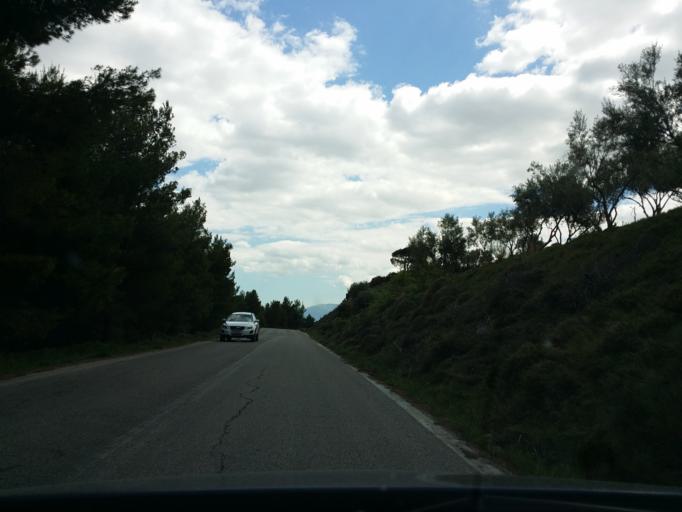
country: GR
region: Attica
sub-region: Nomarchia Dytikis Attikis
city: Fyli
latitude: 38.1209
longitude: 23.6498
